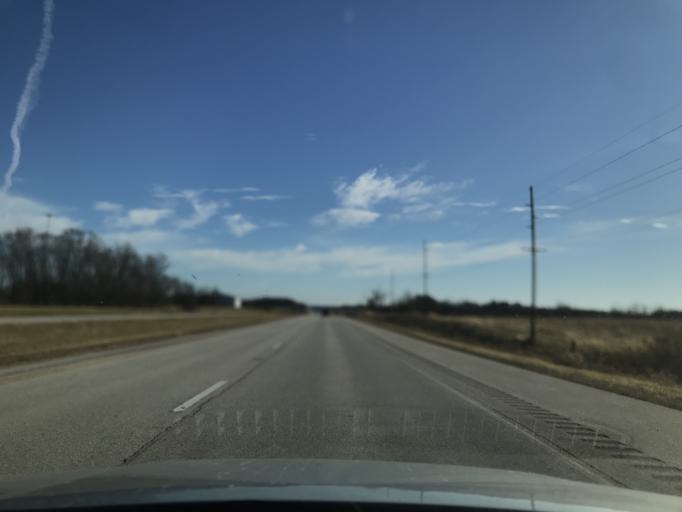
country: US
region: Illinois
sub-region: Hancock County
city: Carthage
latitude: 40.4148
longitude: -91.0421
